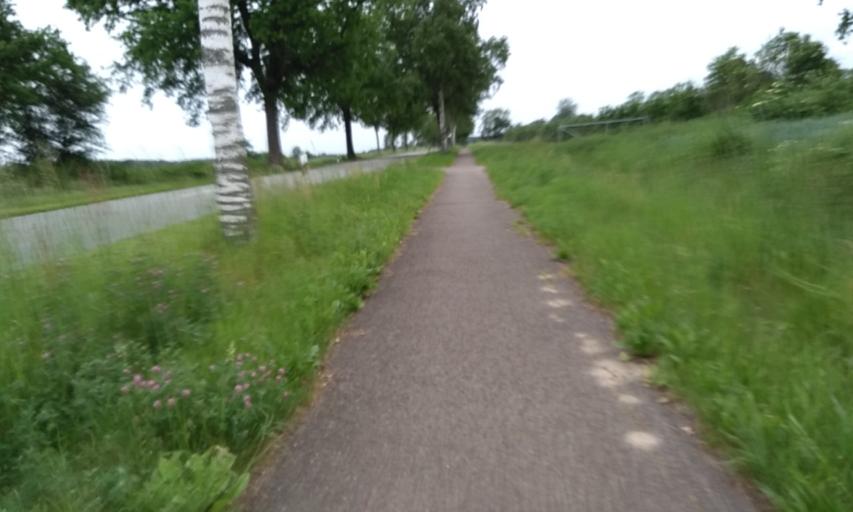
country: DE
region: Lower Saxony
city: Bliedersdorf
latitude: 53.4661
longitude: 9.5791
